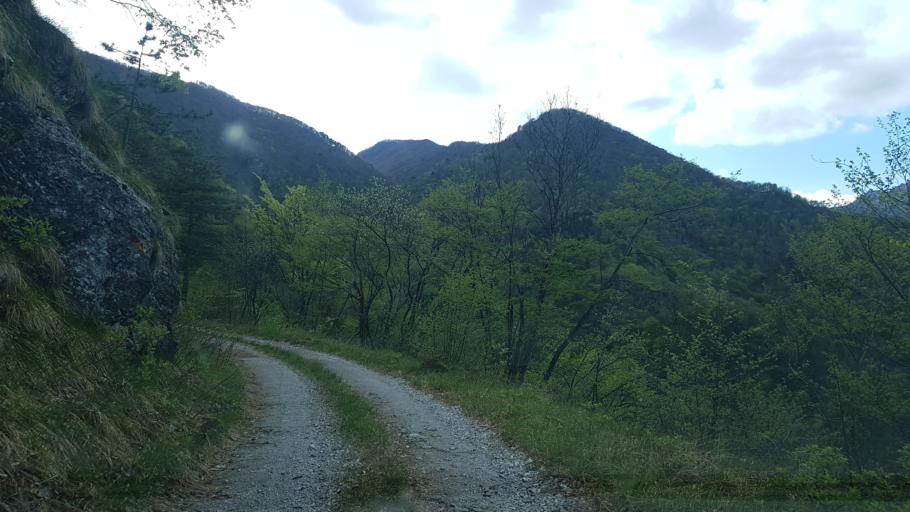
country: IT
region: Friuli Venezia Giulia
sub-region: Provincia di Udine
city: Cavazzo Carnico
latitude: 46.3102
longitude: 13.0079
